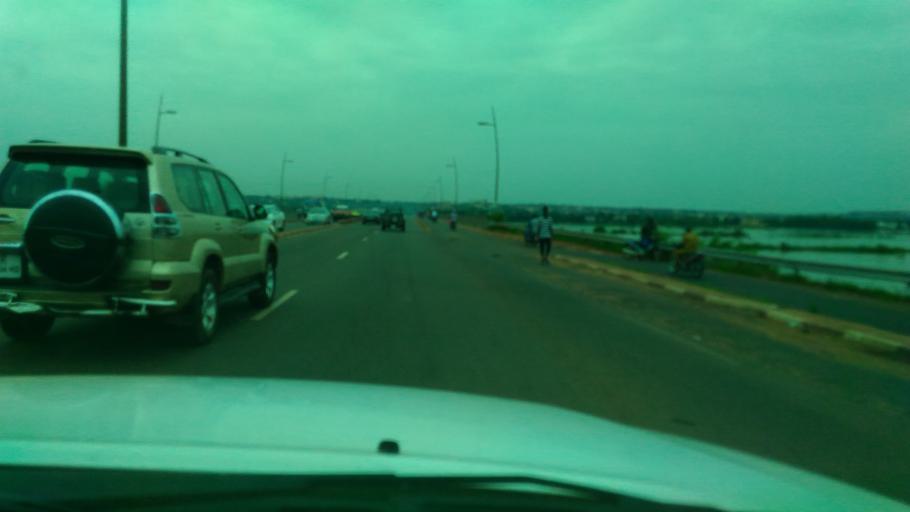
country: ML
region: Bamako
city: Bamako
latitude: 12.6272
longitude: -8.0074
